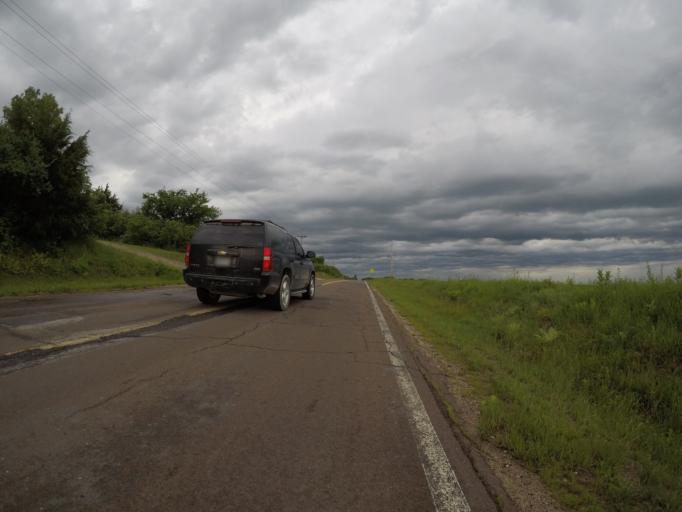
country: US
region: Kansas
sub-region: Shawnee County
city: Auburn
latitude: 38.9644
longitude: -95.9026
